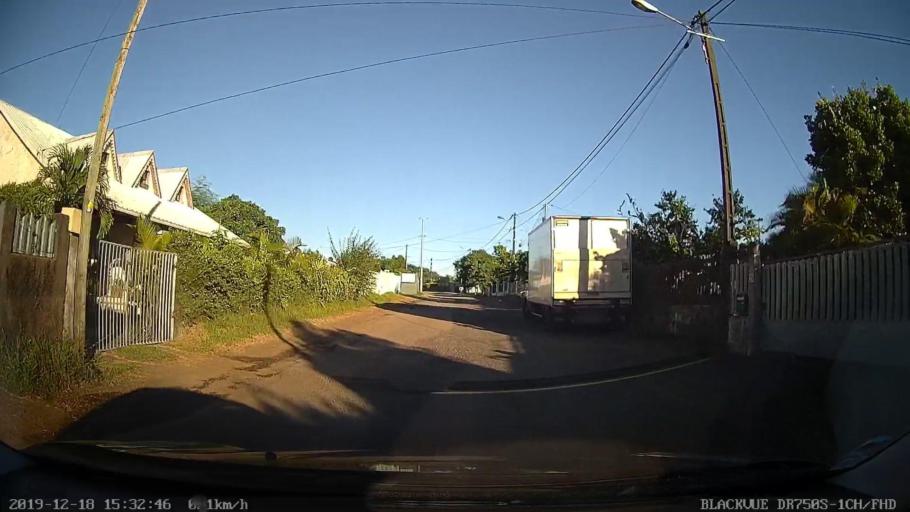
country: RE
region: Reunion
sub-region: Reunion
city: Bras-Panon
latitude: -21.0023
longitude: 55.6707
